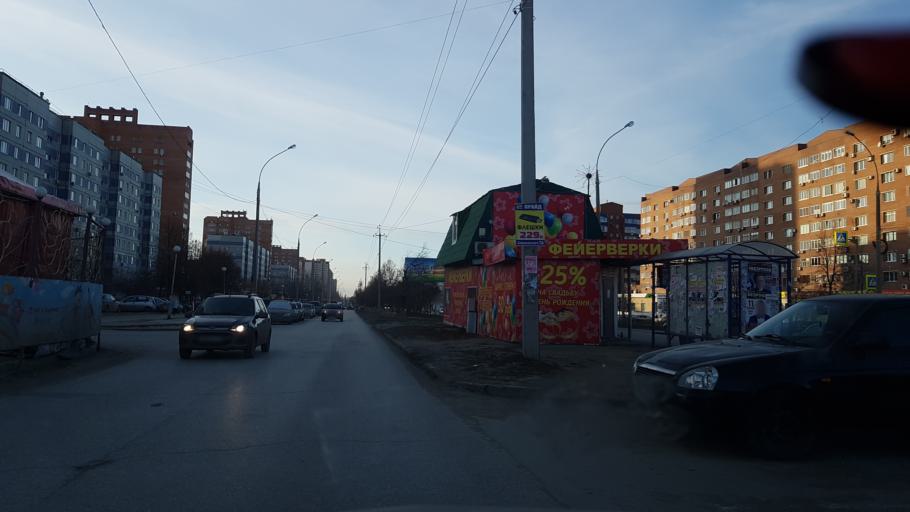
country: RU
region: Samara
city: Tol'yatti
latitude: 53.5411
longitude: 49.3426
